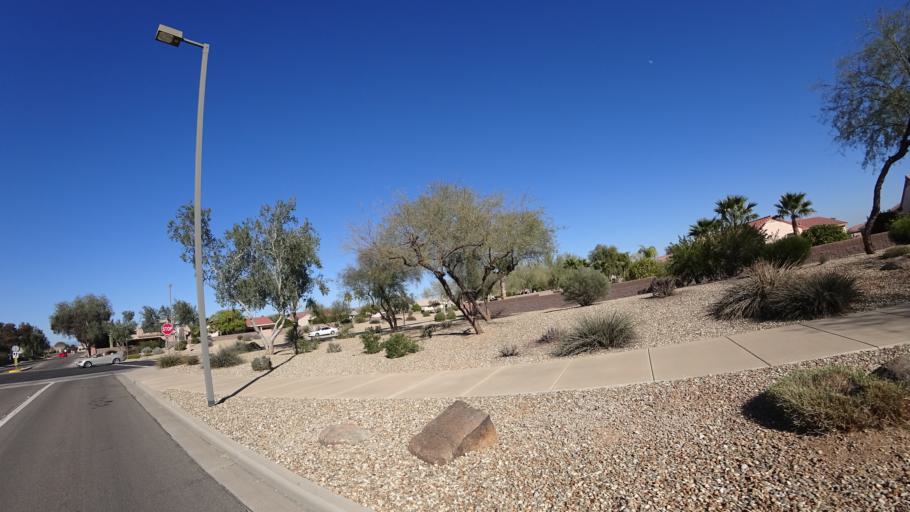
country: US
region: Arizona
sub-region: Maricopa County
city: Sun City West
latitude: 33.6560
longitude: -112.4130
